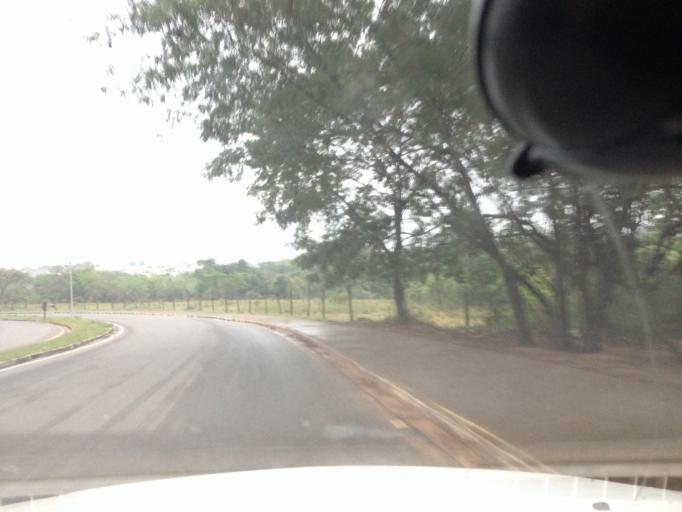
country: BR
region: Sao Paulo
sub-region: Salto
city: Salto
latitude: -23.1976
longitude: -47.2654
